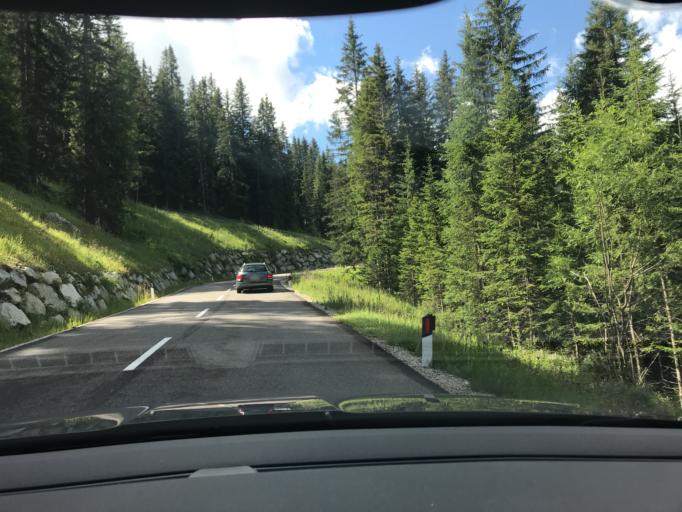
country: IT
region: Veneto
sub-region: Provincia di Belluno
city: Livinallongo del Col di Lana
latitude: 46.5500
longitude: 11.9676
